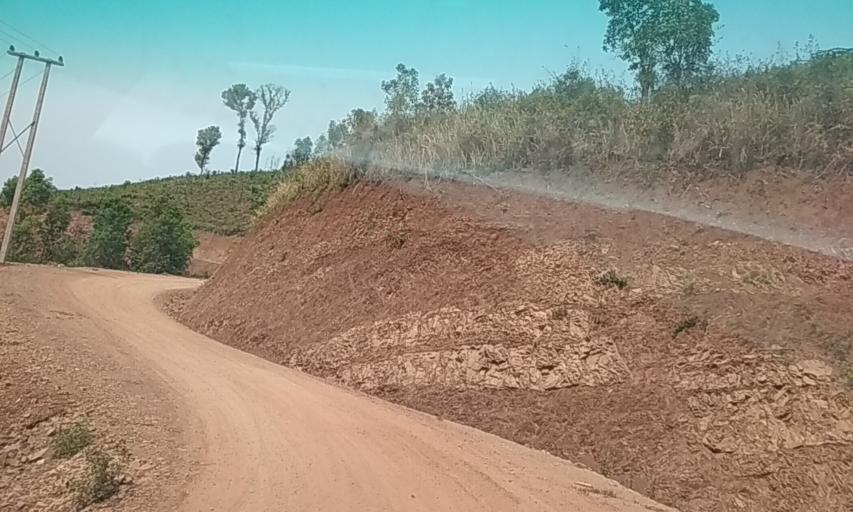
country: VN
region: Huyen Dien Bien
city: Dien Bien Phu
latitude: 21.4830
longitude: 102.7796
